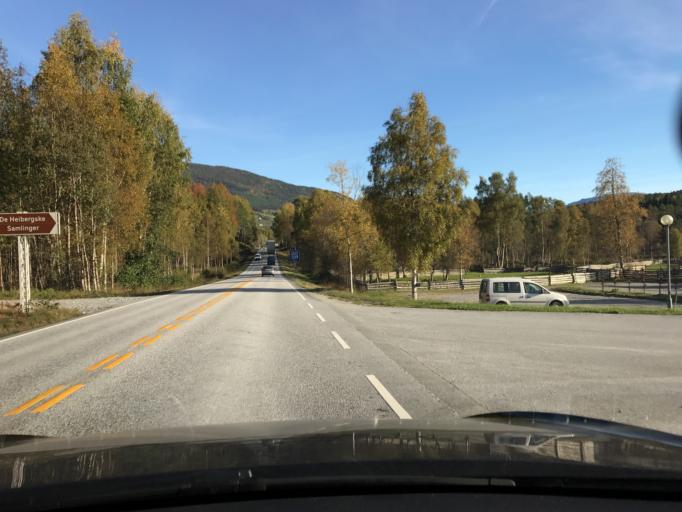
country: NO
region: Sogn og Fjordane
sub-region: Sogndal
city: Sogndalsfjora
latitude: 61.2071
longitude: 7.1902
